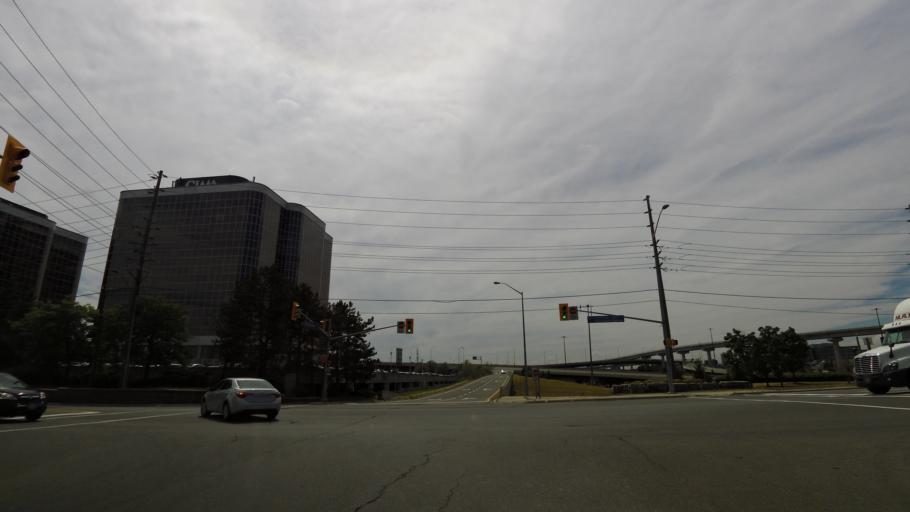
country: CA
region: Ontario
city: Etobicoke
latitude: 43.6890
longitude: -79.6103
